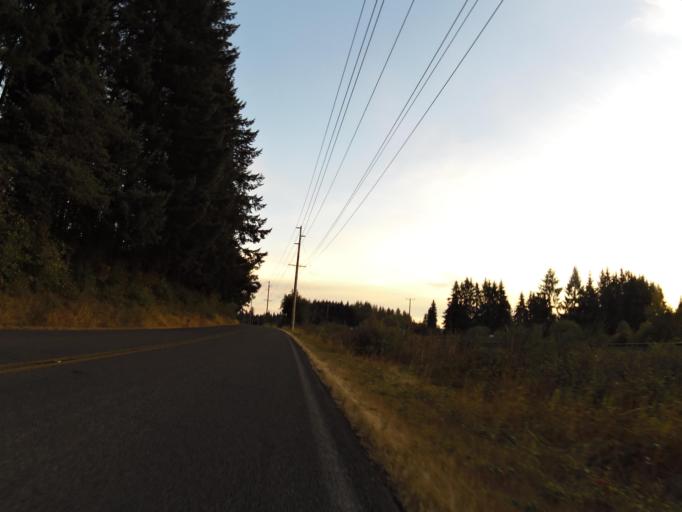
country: US
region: Washington
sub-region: Thurston County
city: Tenino
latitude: 46.8461
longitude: -122.8600
